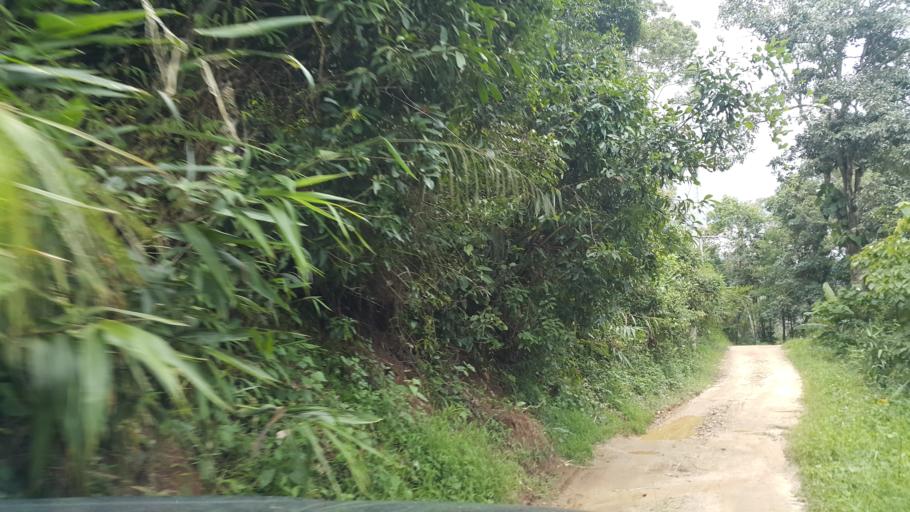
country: TH
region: Lampang
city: Wang Nuea
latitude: 19.0978
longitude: 99.3676
